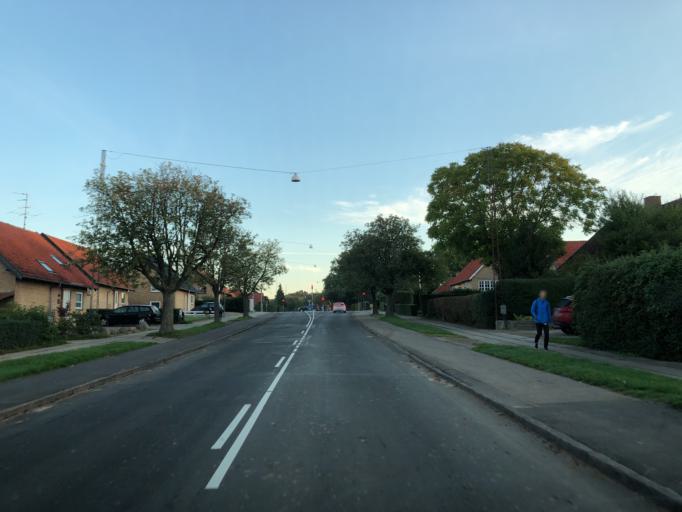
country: DK
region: South Denmark
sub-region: Sonderborg Kommune
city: Sonderborg
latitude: 54.9025
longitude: 9.8101
